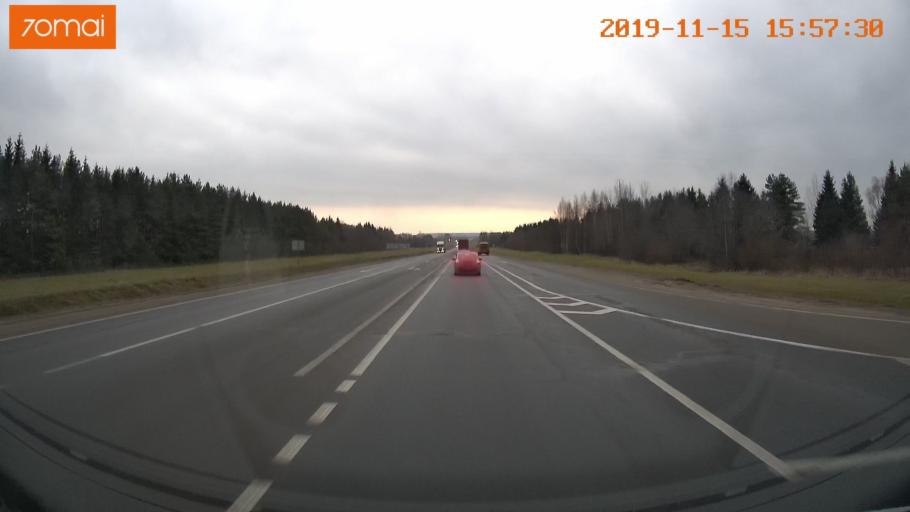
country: RU
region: Jaroslavl
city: Yaroslavl
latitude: 57.8296
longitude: 39.9629
